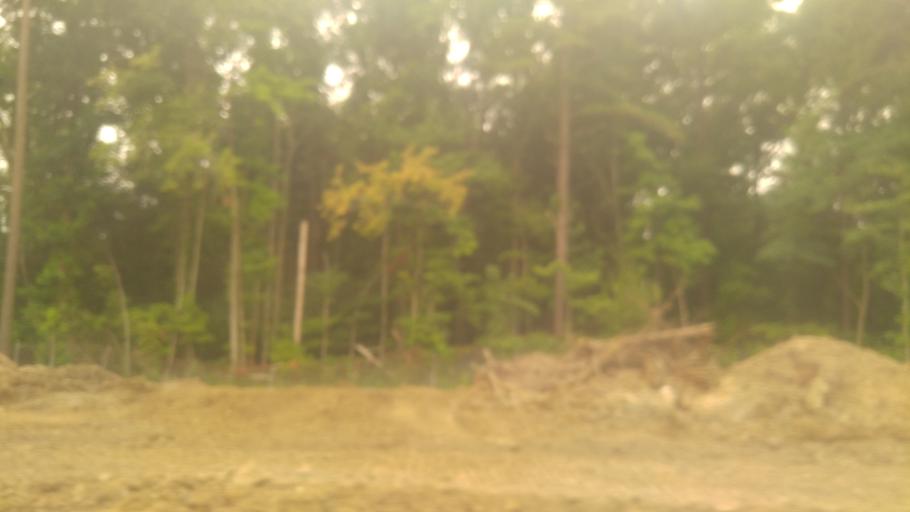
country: US
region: Virginia
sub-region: Henrico County
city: Dumbarton
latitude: 37.6213
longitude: -77.4980
